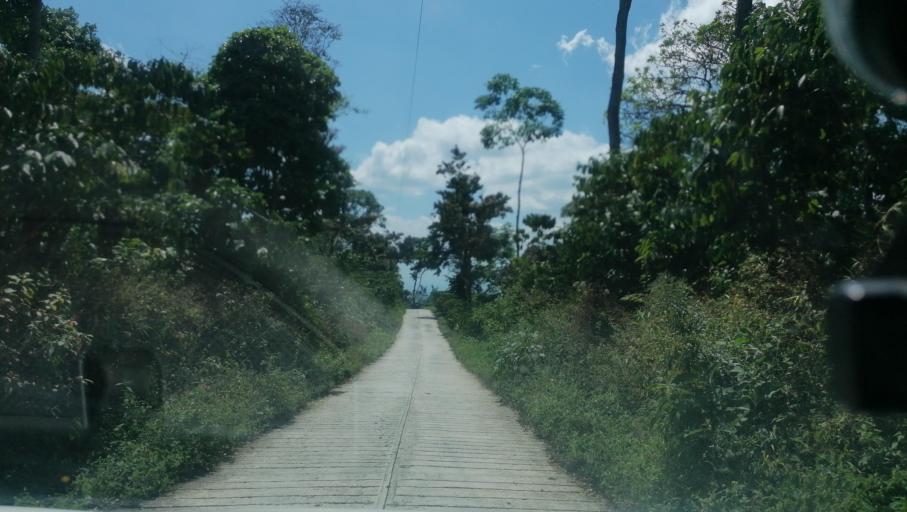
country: MX
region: Chiapas
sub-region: Cacahoatan
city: Benito Juarez
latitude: 15.0486
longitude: -92.1480
